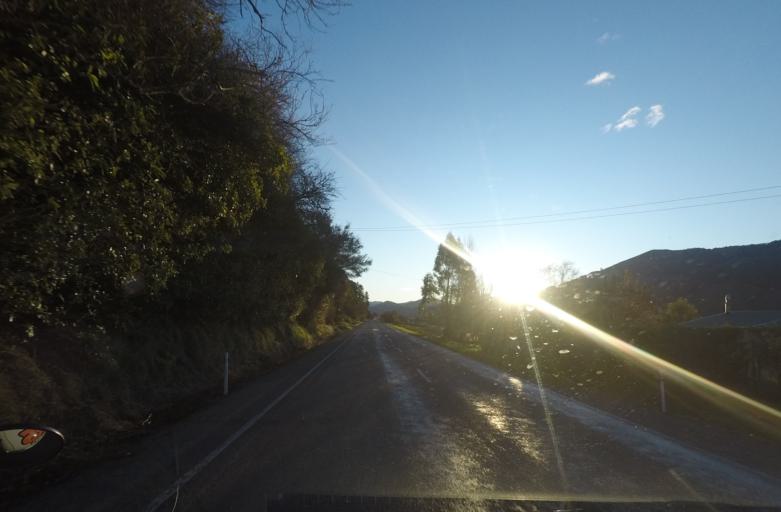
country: NZ
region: Marlborough
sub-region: Marlborough District
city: Picton
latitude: -41.2880
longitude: 173.6989
